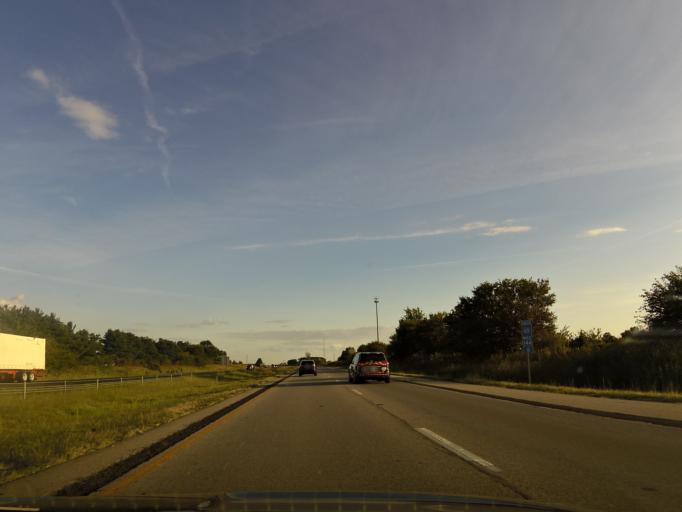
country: US
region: Indiana
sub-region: Boone County
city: Lebanon
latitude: 40.1086
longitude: -86.5127
